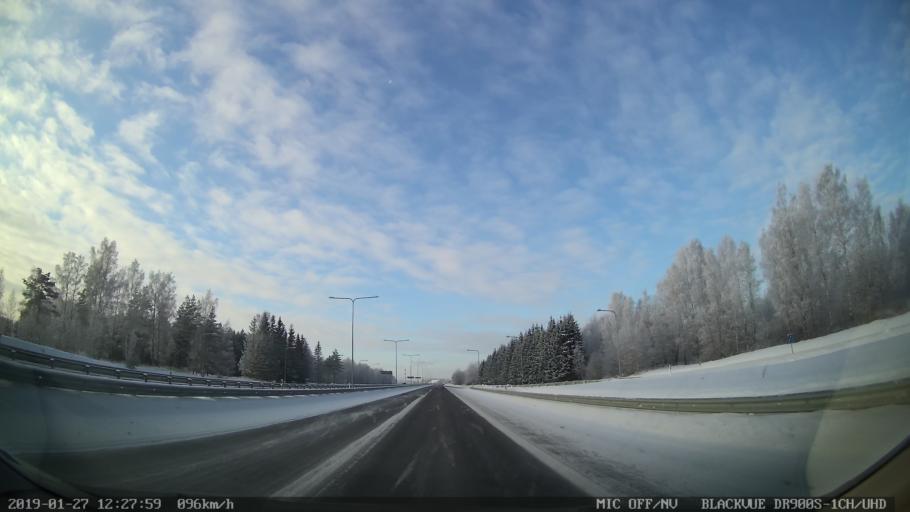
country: EE
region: Harju
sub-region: Maardu linn
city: Maardu
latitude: 59.4523
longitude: 25.0280
